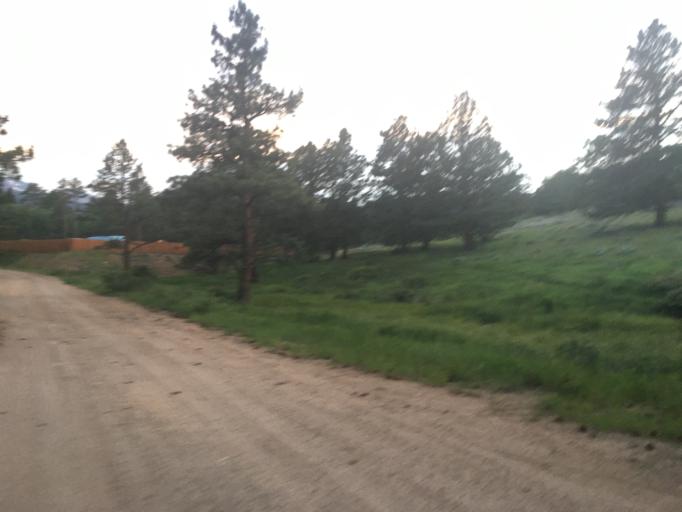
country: US
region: Colorado
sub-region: Larimer County
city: Estes Park
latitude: 40.3451
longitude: -105.5719
